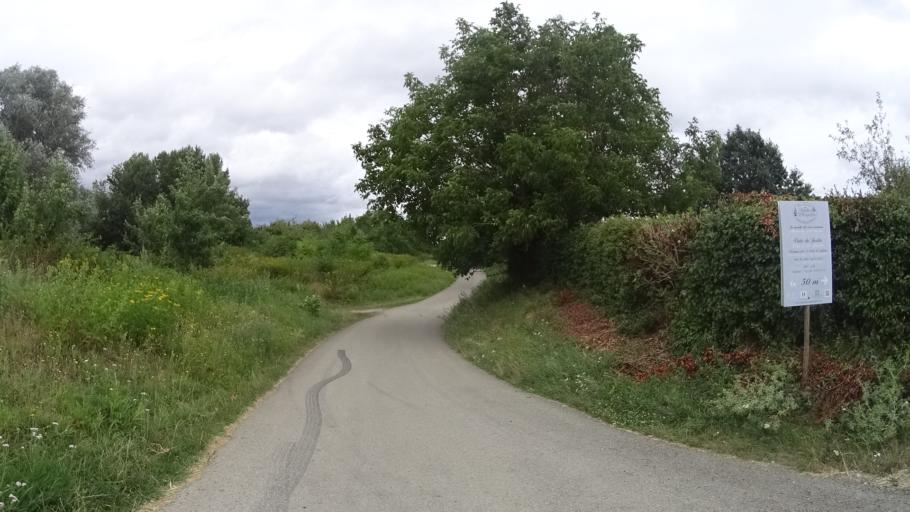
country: FR
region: Centre
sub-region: Departement du Loiret
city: Meung-sur-Loire
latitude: 47.8249
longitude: 1.7064
